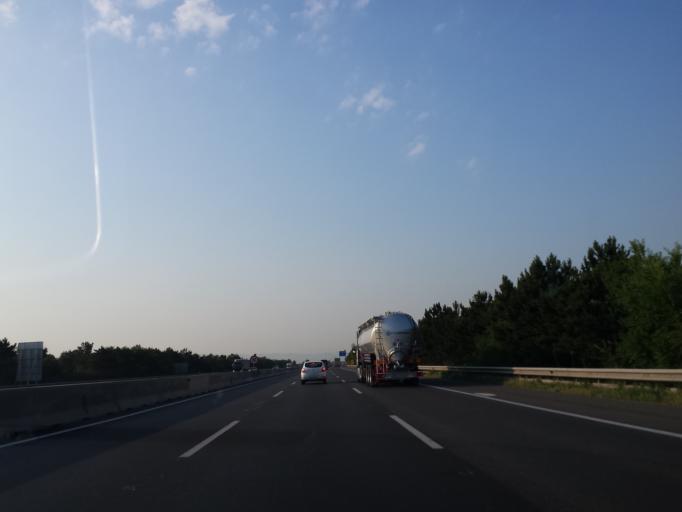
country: AT
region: Lower Austria
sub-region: Politischer Bezirk Wiener Neustadt
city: Weikersdorf am Steinfelde
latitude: 47.8138
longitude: 16.1941
